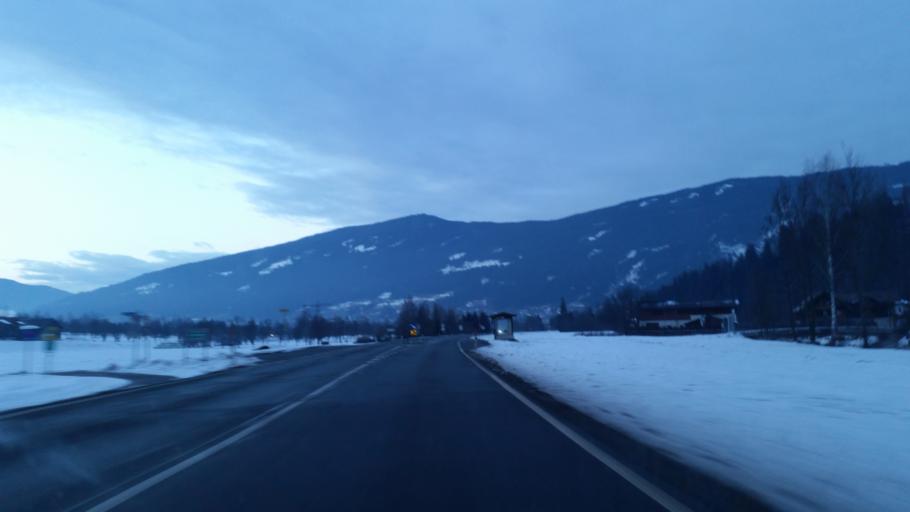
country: AT
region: Salzburg
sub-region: Politischer Bezirk Sankt Johann im Pongau
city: Radstadt
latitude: 47.3683
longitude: 13.4825
